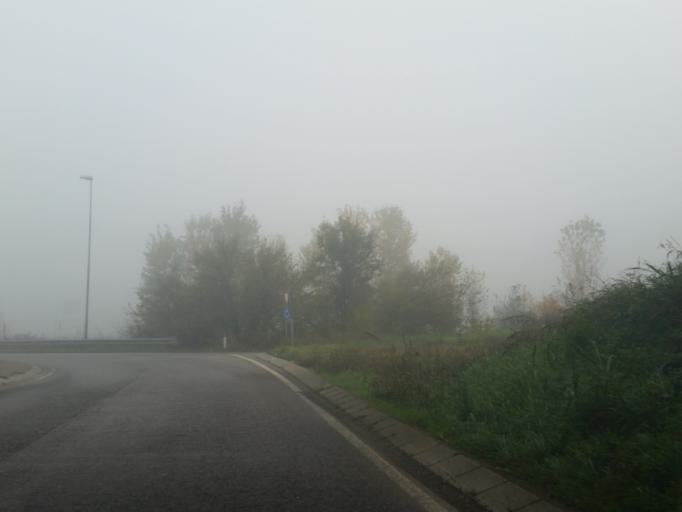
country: IT
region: Lombardy
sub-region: Provincia di Brescia
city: Barbariga
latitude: 45.3794
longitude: 10.0577
